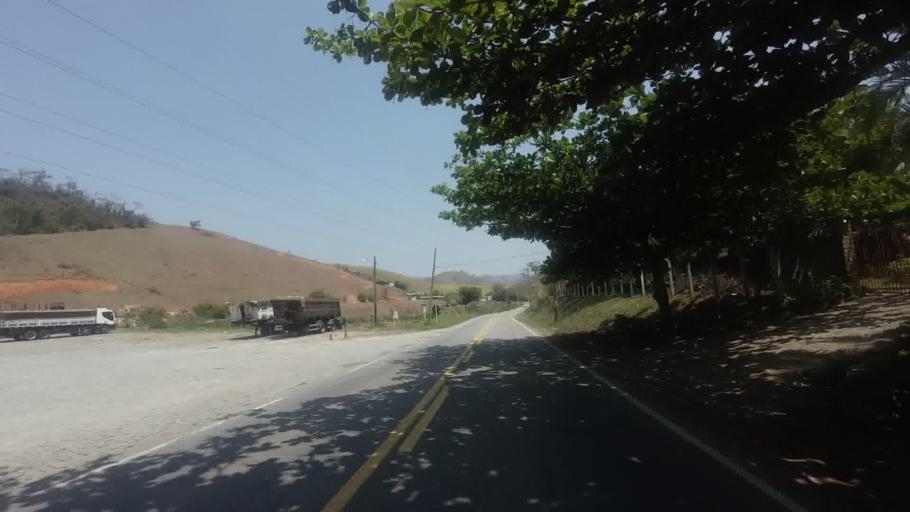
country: BR
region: Espirito Santo
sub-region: Cachoeiro De Itapemirim
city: Cachoeiro de Itapemirim
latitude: -20.8564
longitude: -41.0692
